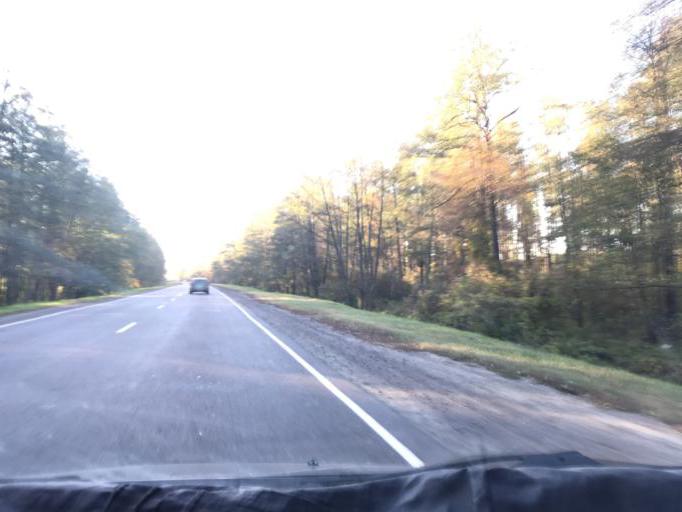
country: BY
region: Gomel
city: Pyetrykaw
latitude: 52.2737
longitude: 28.2561
